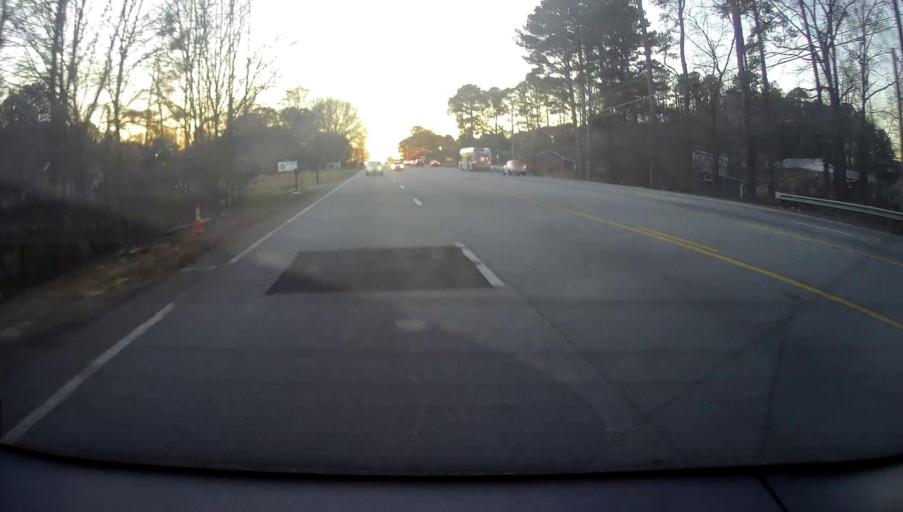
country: US
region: Georgia
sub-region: Clayton County
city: Riverdale
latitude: 33.5508
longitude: -84.4438
